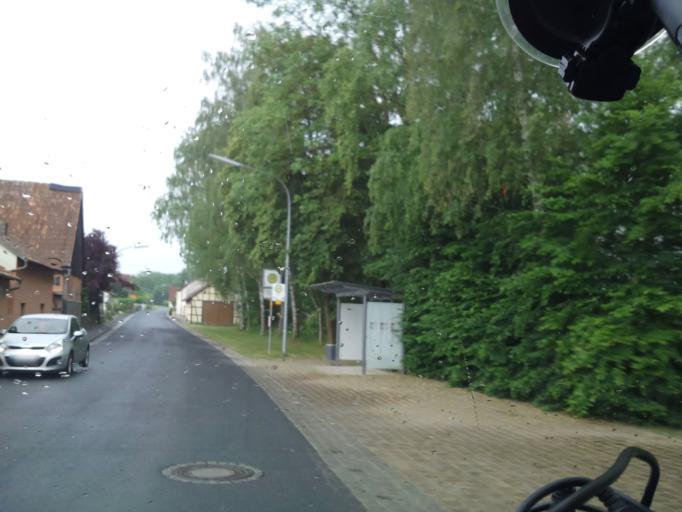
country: DE
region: Bavaria
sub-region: Regierungsbezirk Unterfranken
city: Hochheim
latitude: 50.3631
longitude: 10.4501
